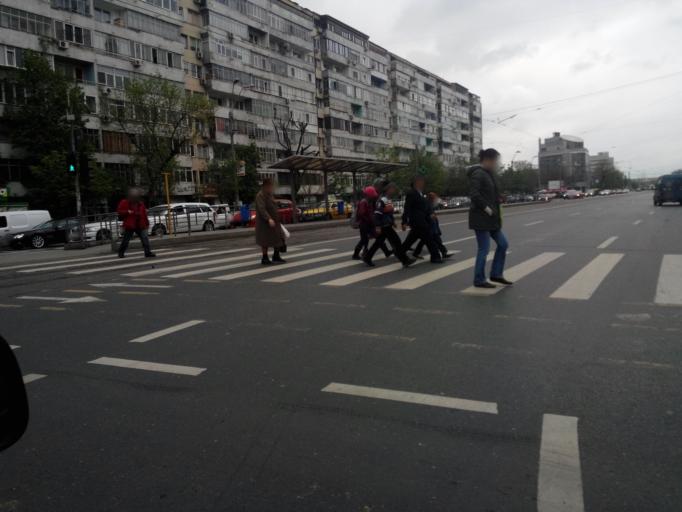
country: RO
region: Bucuresti
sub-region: Municipiul Bucuresti
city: Bucharest
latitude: 44.4375
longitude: 26.1362
